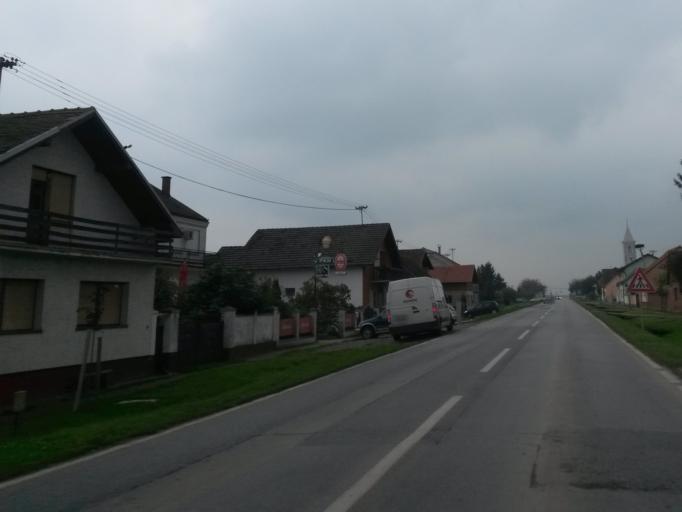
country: HR
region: Osjecko-Baranjska
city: Viskovci
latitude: 45.3523
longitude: 18.4237
